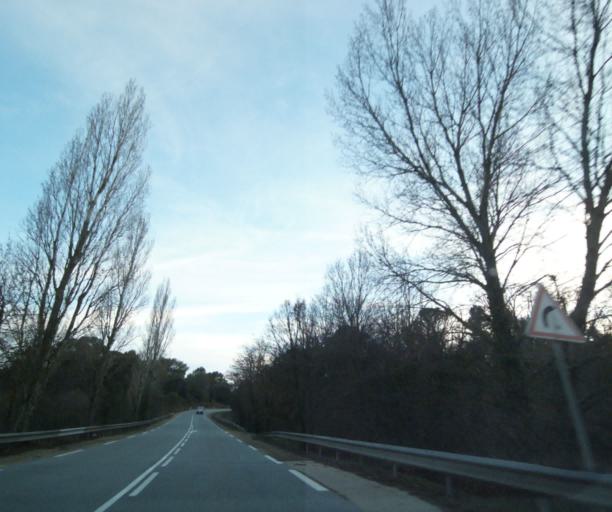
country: FR
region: Provence-Alpes-Cote d'Azur
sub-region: Departement du Var
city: La Motte
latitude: 43.4889
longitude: 6.5117
